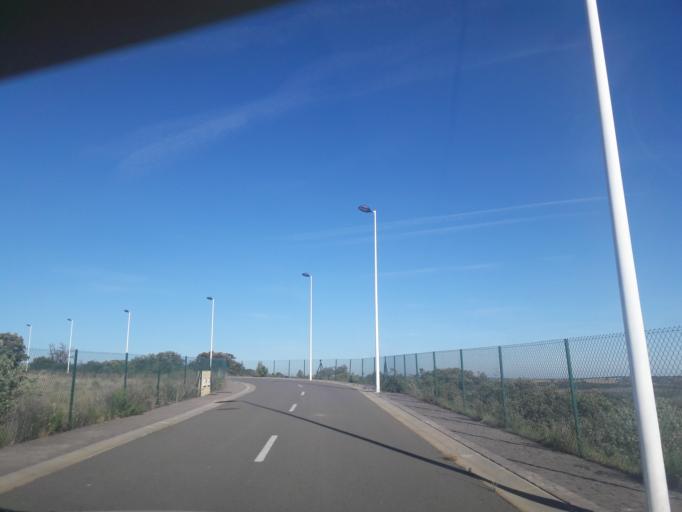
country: ES
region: Castille and Leon
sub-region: Provincia de Salamanca
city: Mozarbez
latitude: 40.8084
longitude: -5.6474
